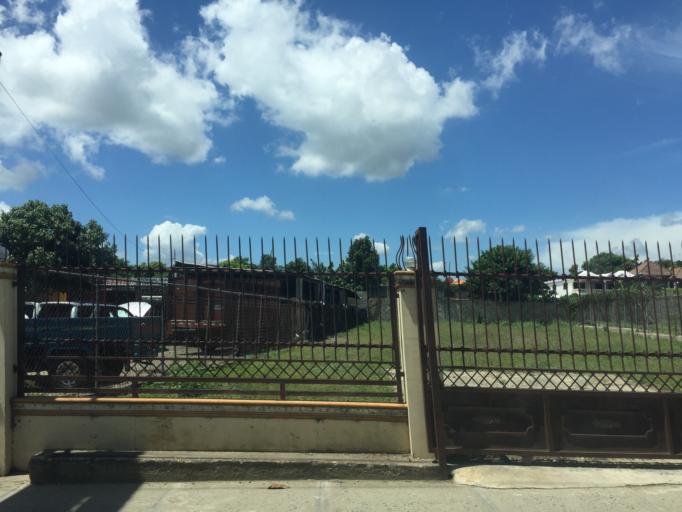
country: DO
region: Santiago
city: Santiago de los Caballeros
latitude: 19.4408
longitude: -70.7286
